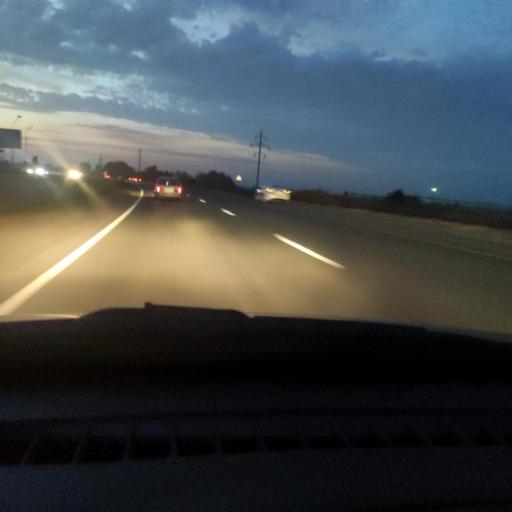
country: RU
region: Samara
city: Tol'yatti
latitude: 53.5661
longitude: 49.4933
